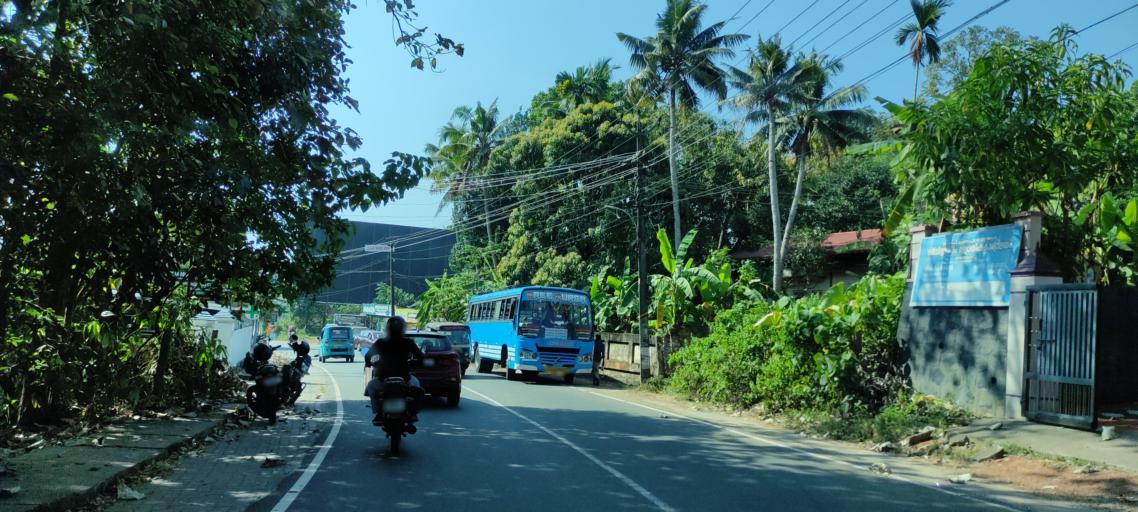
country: IN
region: Kerala
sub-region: Kollam
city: Panmana
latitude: 9.0454
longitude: 76.6266
